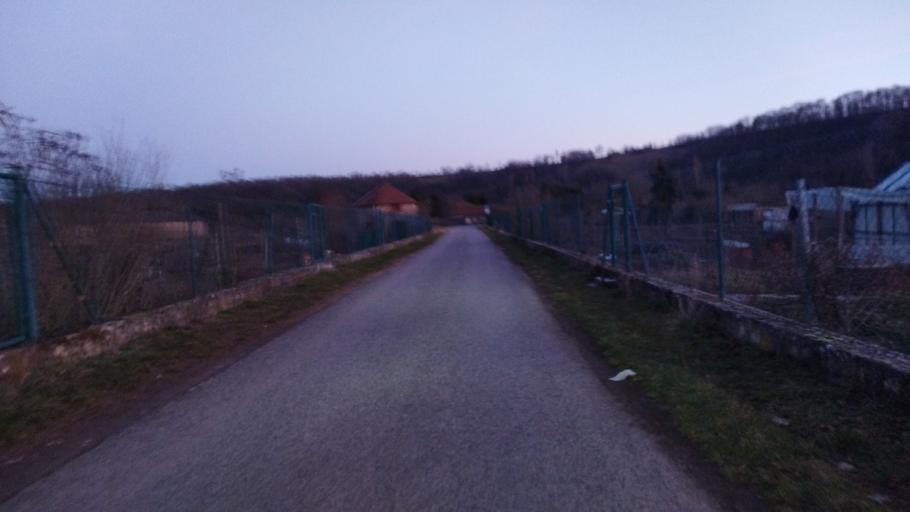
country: DE
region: Bavaria
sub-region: Regierungsbezirk Unterfranken
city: Nordheim
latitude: 49.8744
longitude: 10.1646
